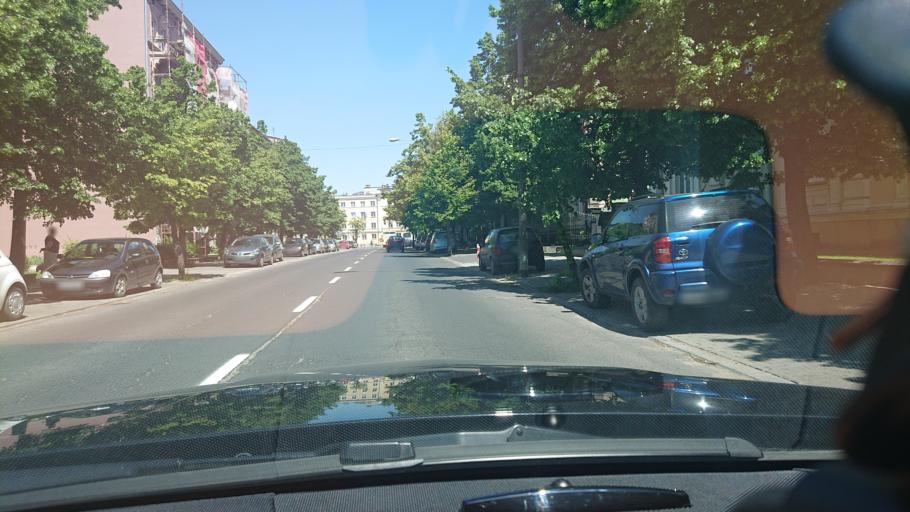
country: PL
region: Greater Poland Voivodeship
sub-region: Powiat gnieznienski
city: Gniezno
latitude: 52.5317
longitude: 17.6024
